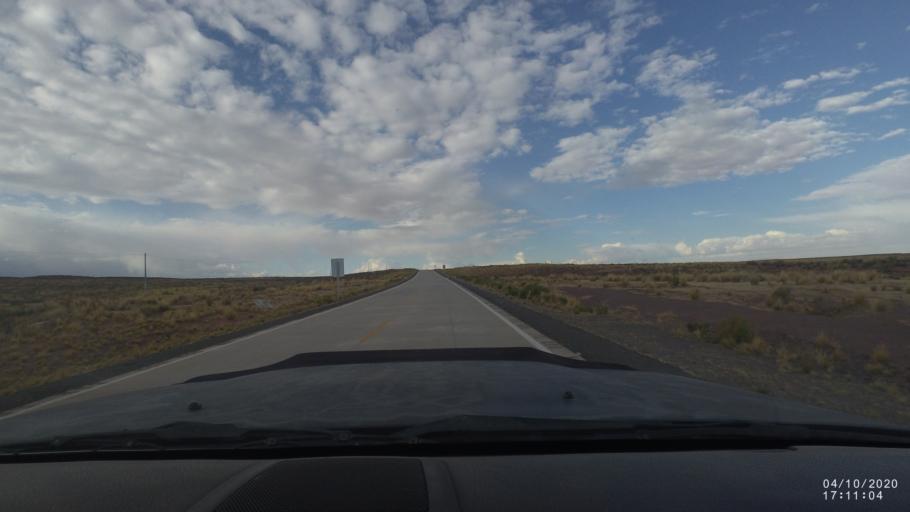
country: BO
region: Oruro
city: Oruro
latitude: -18.3239
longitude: -67.5789
